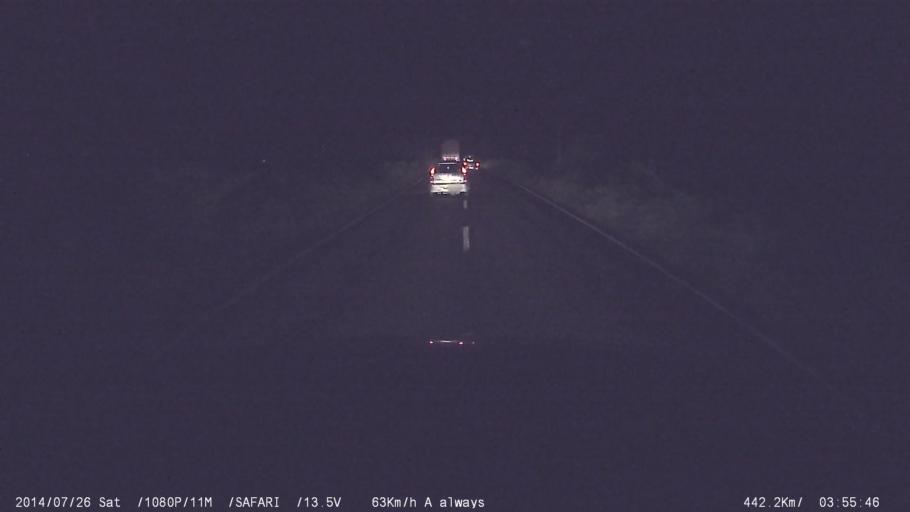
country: IN
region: Kerala
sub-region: Thrissur District
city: Chelakara
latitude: 10.5621
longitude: 76.3483
